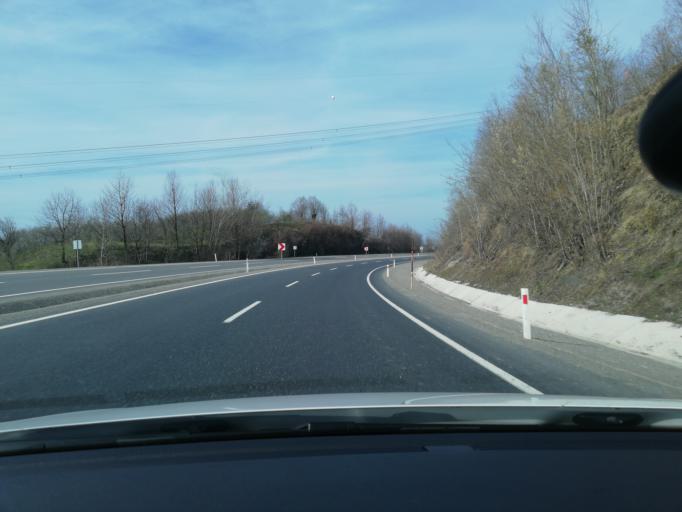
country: TR
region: Zonguldak
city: Kozlu
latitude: 41.3401
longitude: 31.6293
